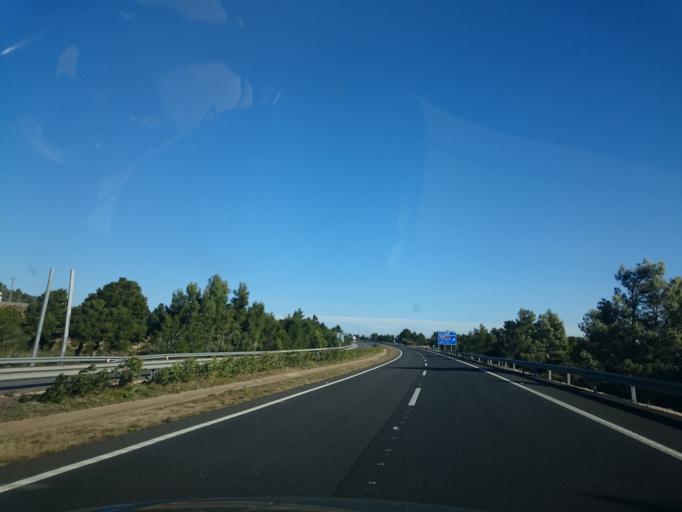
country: ES
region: Catalonia
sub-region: Provincia de Tarragona
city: Colldejou
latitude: 40.9927
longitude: 0.9046
